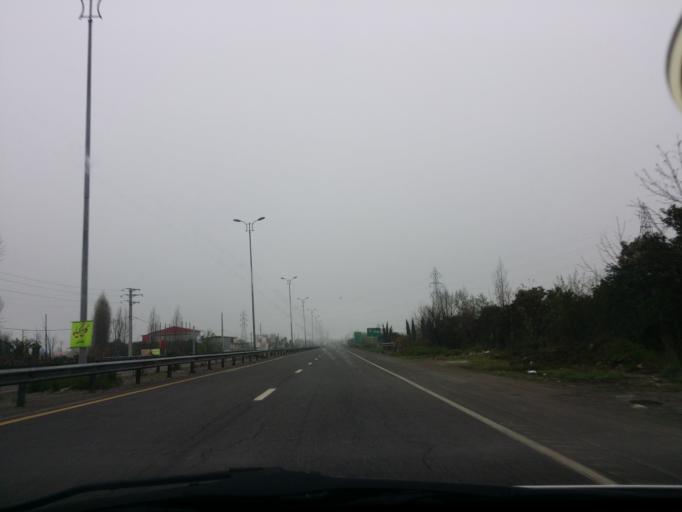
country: IR
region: Mazandaran
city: Tonekabon
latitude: 36.8254
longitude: 50.8449
